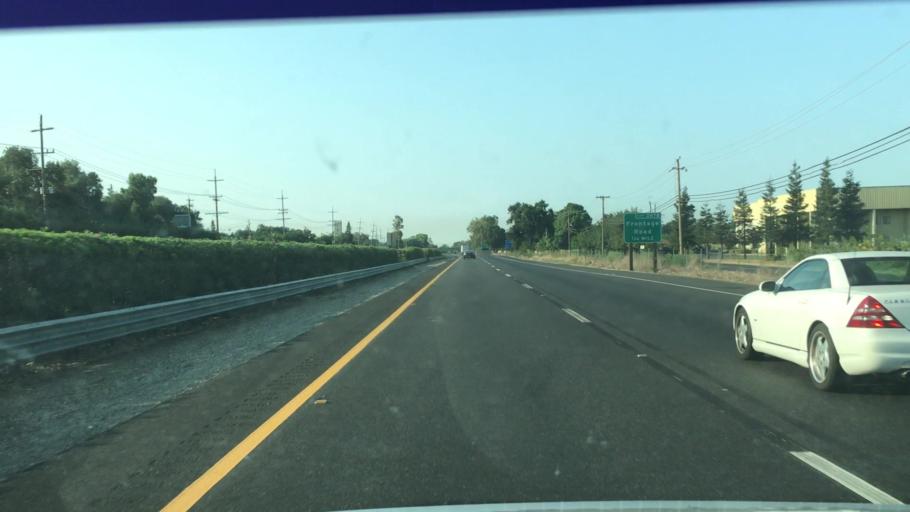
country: US
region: California
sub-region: San Joaquin County
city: Lodi
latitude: 38.1571
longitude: -121.2618
